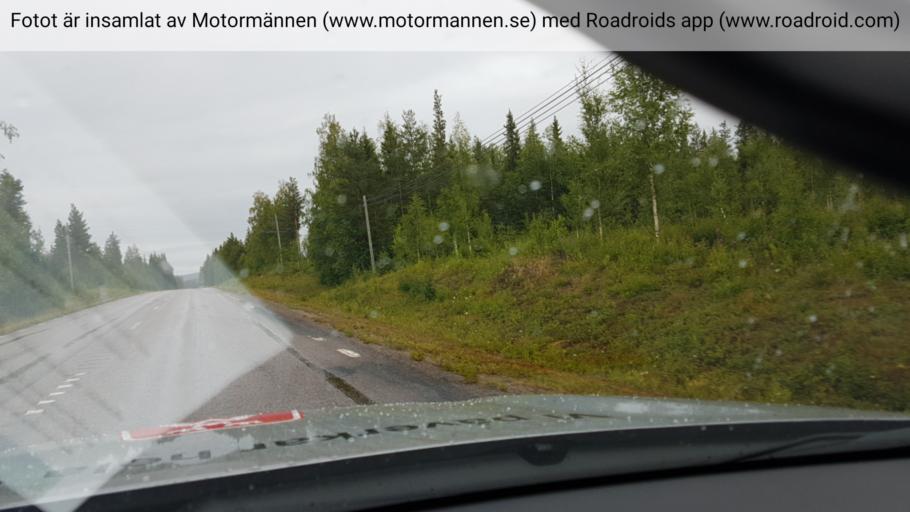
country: SE
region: Norrbotten
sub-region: Alvsbyns Kommun
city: AElvsbyn
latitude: 66.2147
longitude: 20.8737
